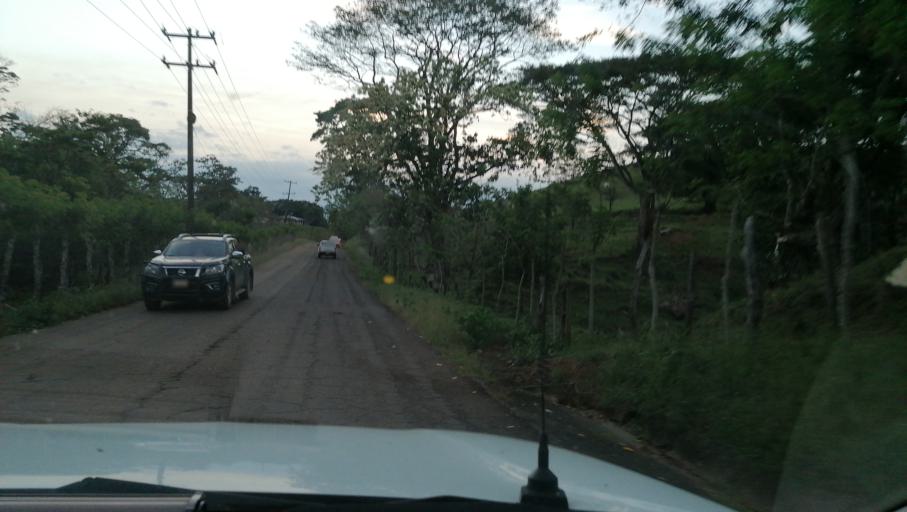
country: MX
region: Chiapas
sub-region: Ostuacan
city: Nuevo Juan del Grijalva
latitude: 17.4466
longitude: -93.3564
